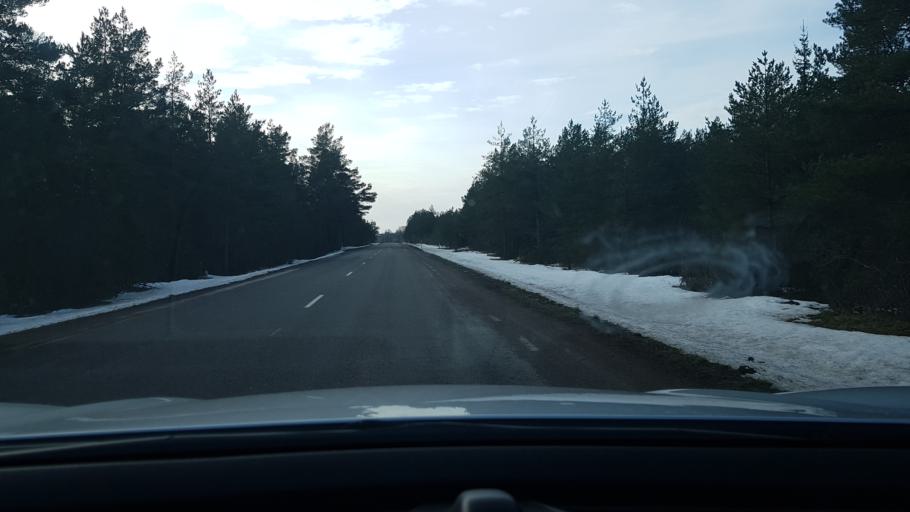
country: EE
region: Saare
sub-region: Kuressaare linn
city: Kuressaare
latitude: 58.3227
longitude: 22.5513
